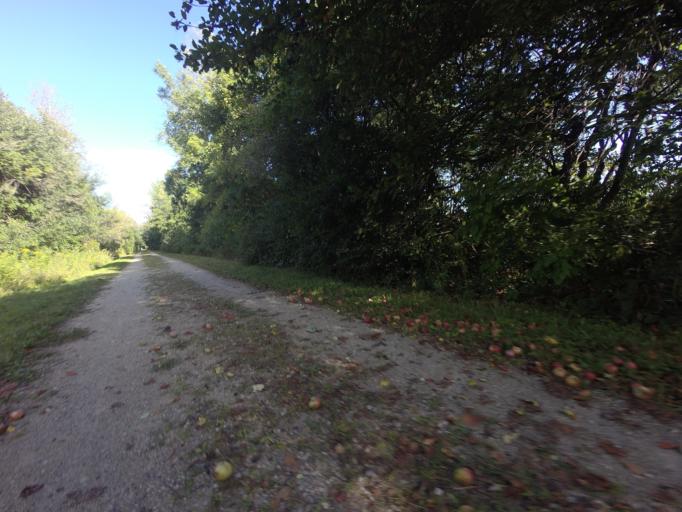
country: CA
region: Ontario
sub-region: Wellington County
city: Guelph
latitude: 43.6615
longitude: -80.4308
